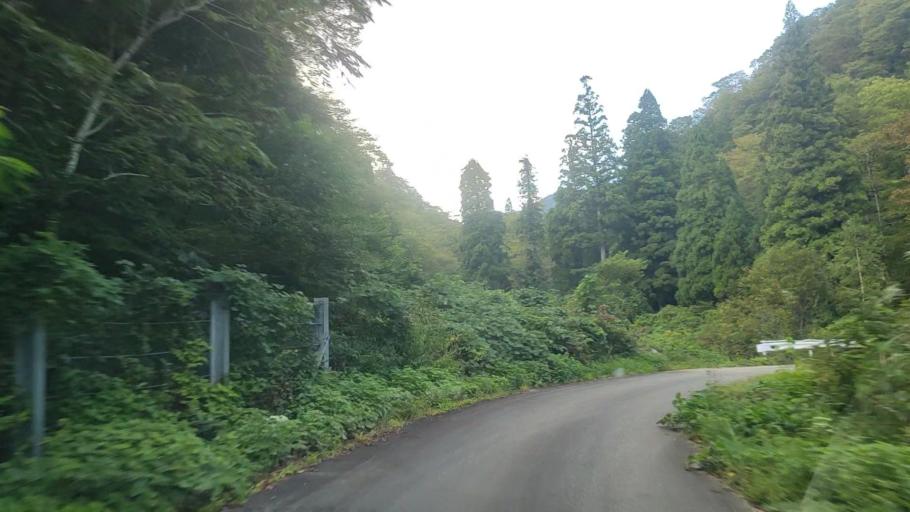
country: JP
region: Gifu
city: Takayama
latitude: 36.3158
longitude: 137.0841
